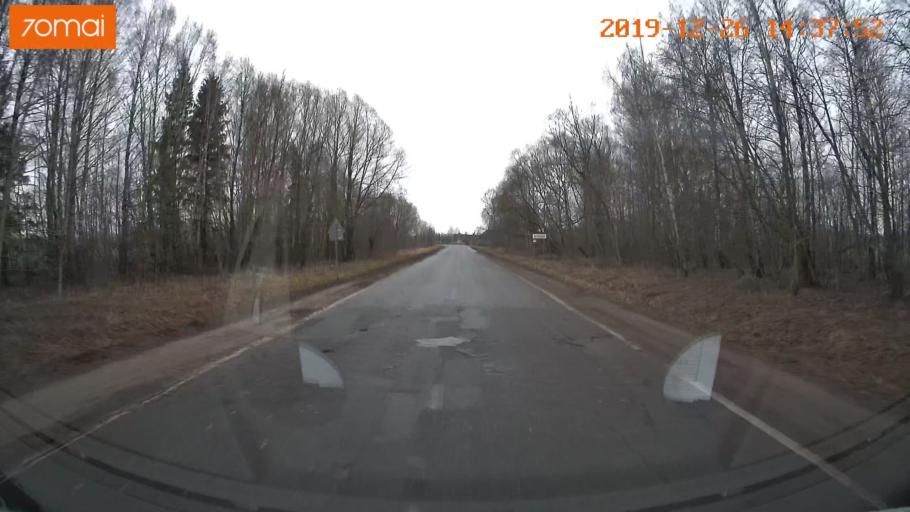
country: RU
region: Jaroslavl
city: Poshekhon'ye
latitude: 58.3989
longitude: 38.9716
